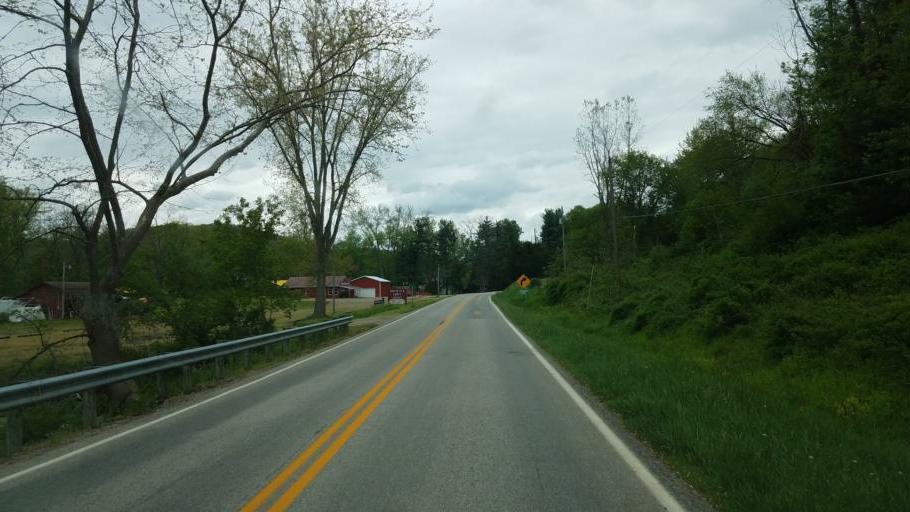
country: US
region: Ohio
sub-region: Ashland County
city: Loudonville
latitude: 40.6152
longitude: -82.2511
